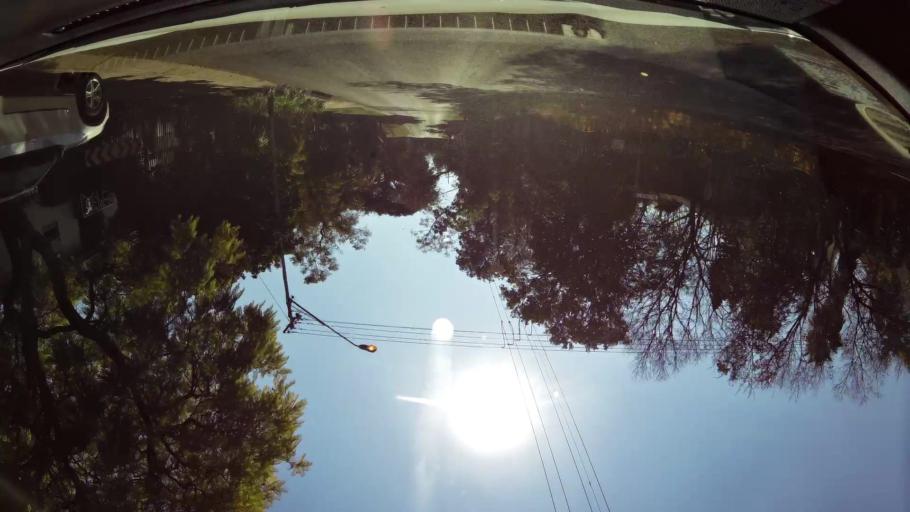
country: ZA
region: Gauteng
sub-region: City of Tshwane Metropolitan Municipality
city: Pretoria
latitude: -25.7778
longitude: 28.2631
